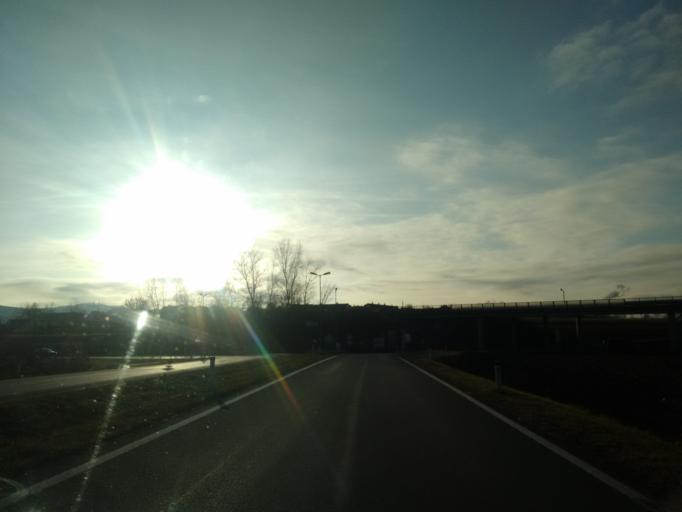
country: AT
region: Lower Austria
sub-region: Politischer Bezirk Melk
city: Emmersdorf an der Donau
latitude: 48.2330
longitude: 15.3491
